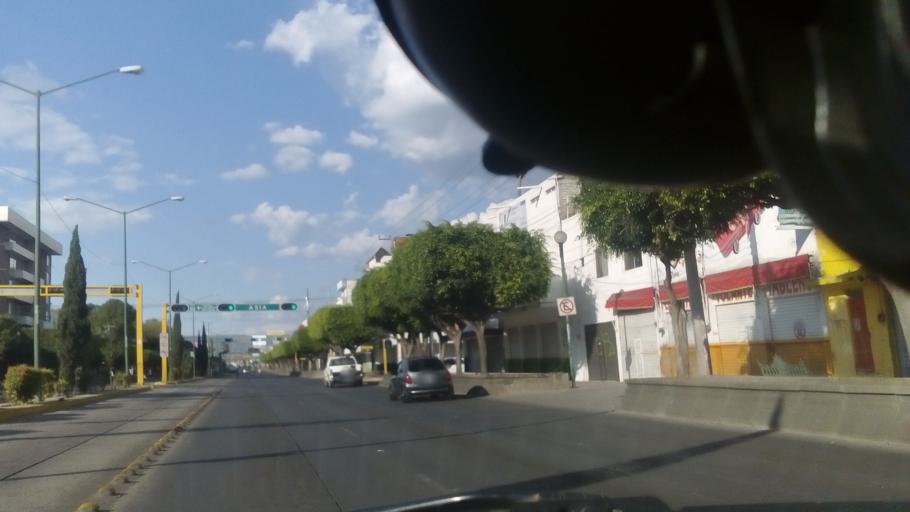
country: MX
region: Guanajuato
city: Leon
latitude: 21.1350
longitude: -101.6873
